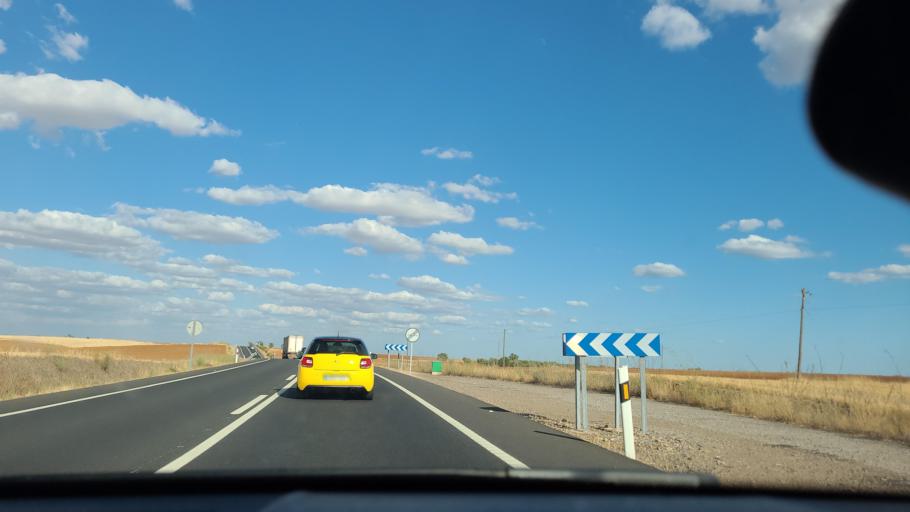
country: ES
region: Extremadura
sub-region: Provincia de Badajoz
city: Berlanga
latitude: 38.2666
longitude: -5.7814
